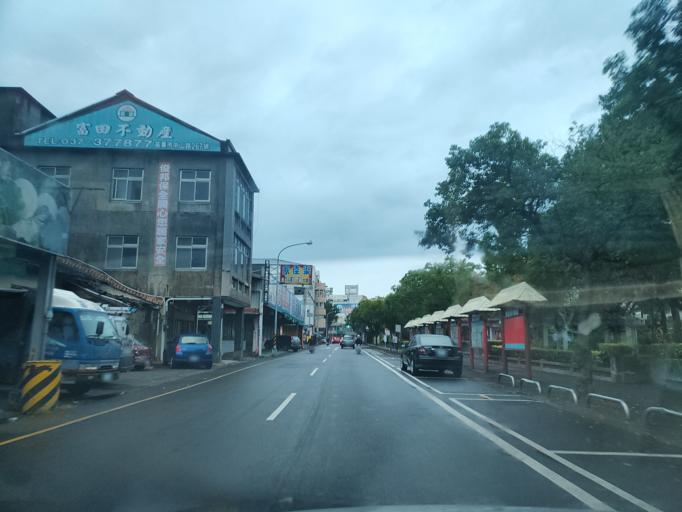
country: TW
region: Taiwan
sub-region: Miaoli
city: Miaoli
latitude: 24.5630
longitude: 120.8230
